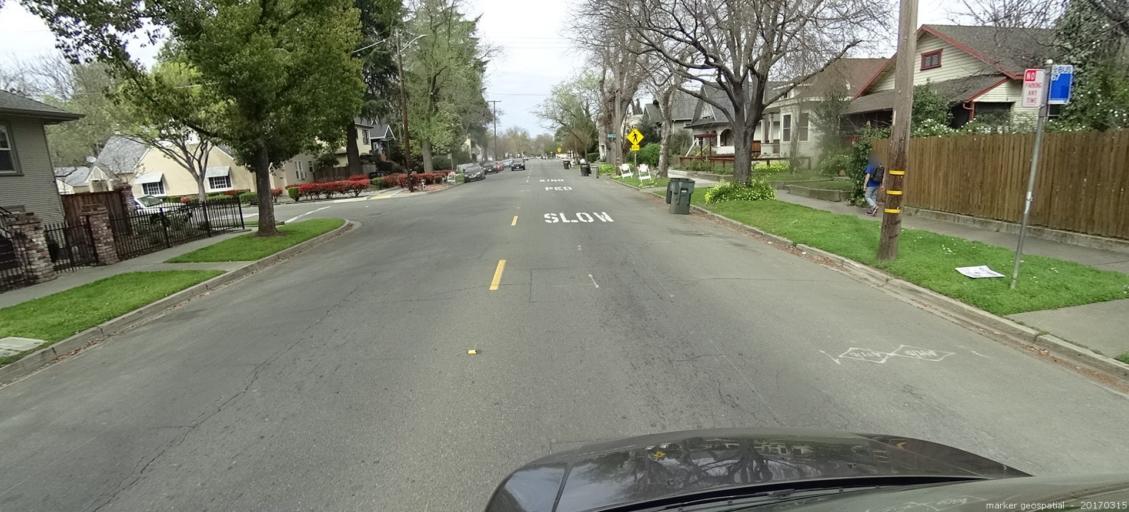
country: US
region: California
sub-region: Sacramento County
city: Sacramento
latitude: 38.5506
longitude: -121.4758
